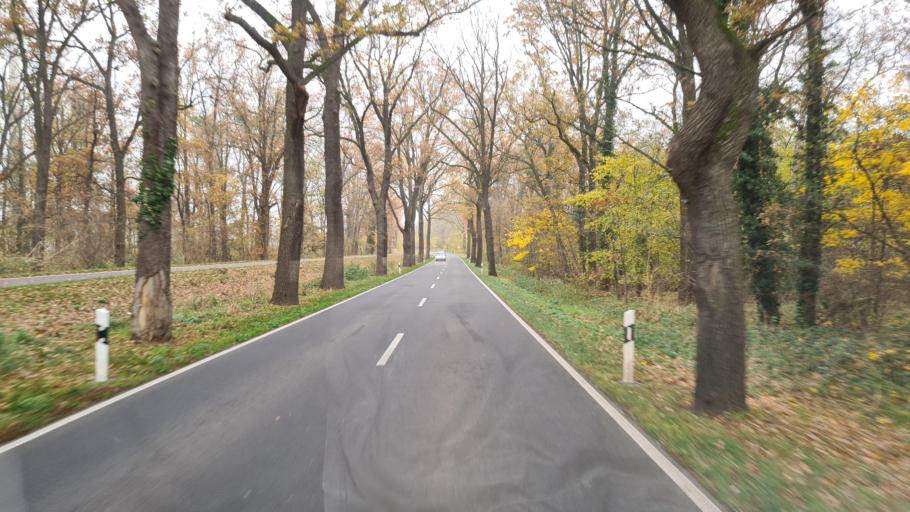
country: DE
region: Brandenburg
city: Gross Kreutz
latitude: 52.3967
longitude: 12.7684
